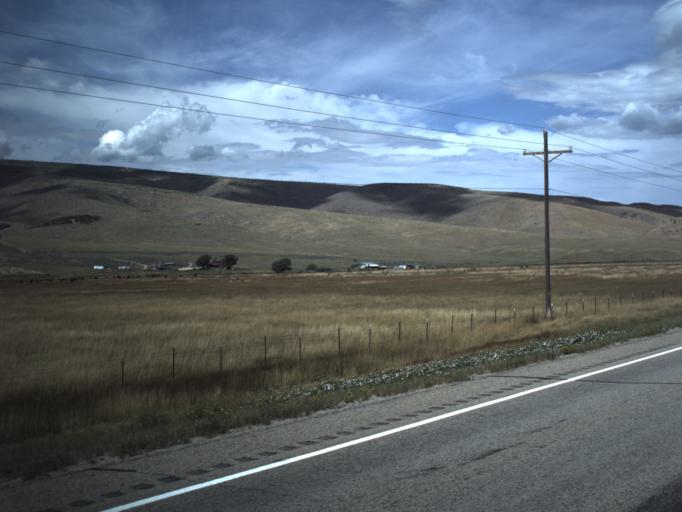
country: US
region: Utah
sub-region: Sanpete County
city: Fairview
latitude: 39.7987
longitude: -111.5004
